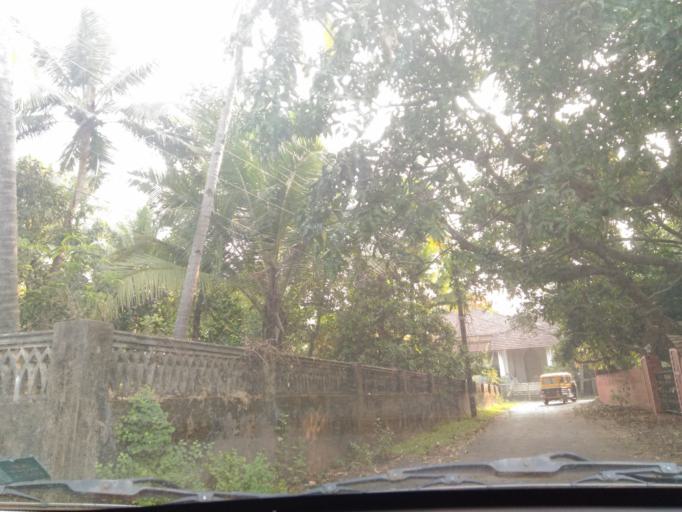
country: IN
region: Goa
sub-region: South Goa
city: Cuncolim
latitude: 15.1749
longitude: 73.9751
